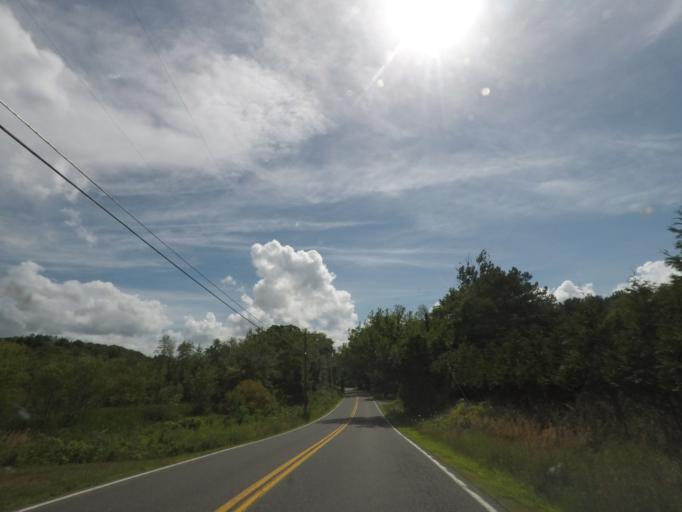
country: US
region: New York
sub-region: Rensselaer County
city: Wynantskill
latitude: 42.7084
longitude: -73.6091
